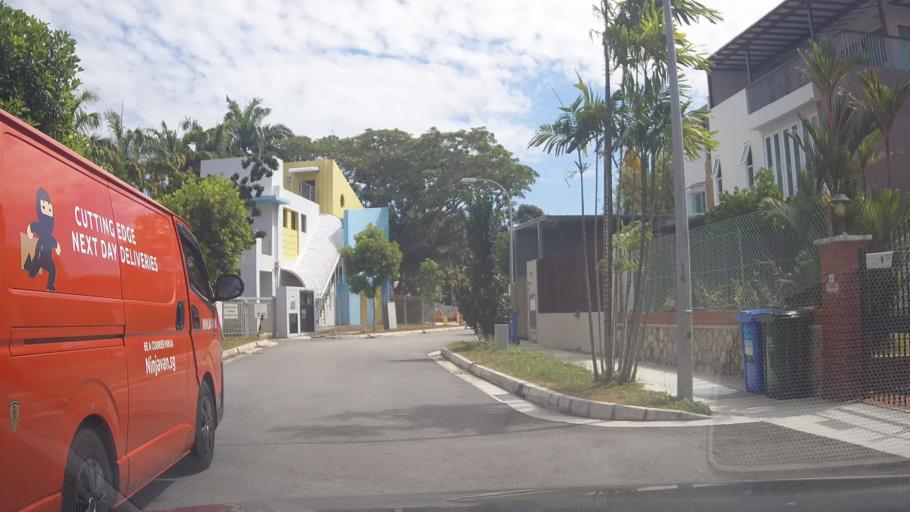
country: SG
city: Singapore
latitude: 1.3617
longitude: 103.9654
